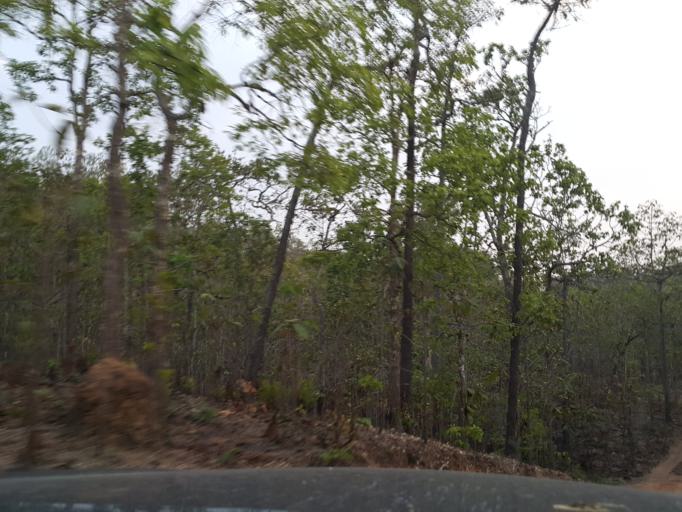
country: TH
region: Lamphun
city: Thung Hua Chang
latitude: 17.9054
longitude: 99.0818
